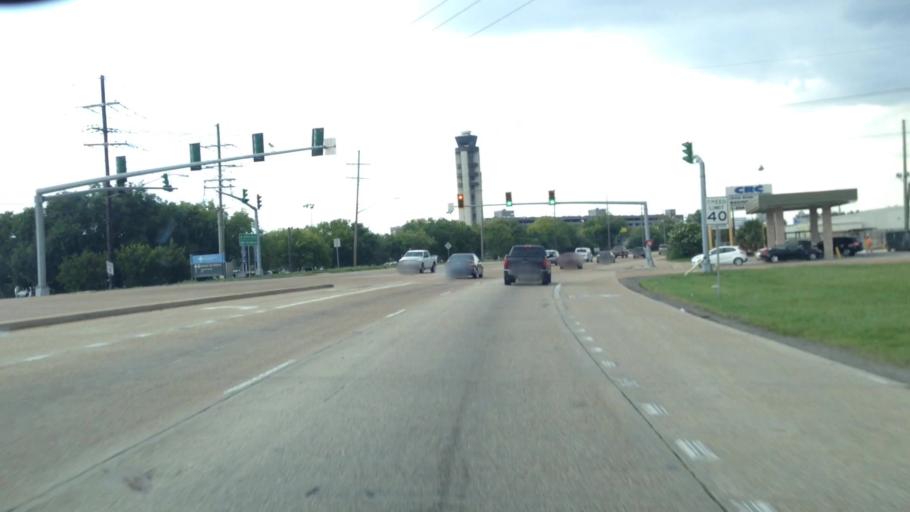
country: US
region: Louisiana
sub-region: Jefferson Parish
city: Kenner
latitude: 29.9834
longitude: -90.2639
